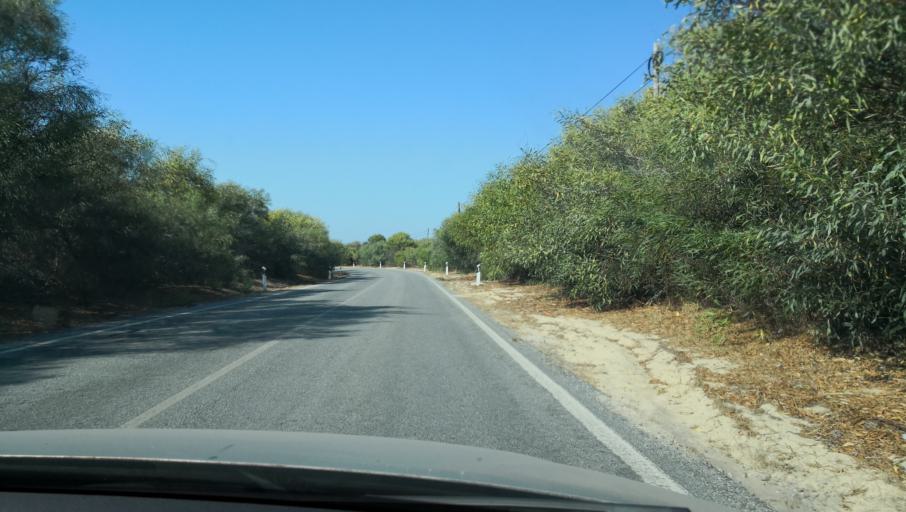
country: PT
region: Setubal
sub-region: Setubal
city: Setubal
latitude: 38.3884
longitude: -8.8002
